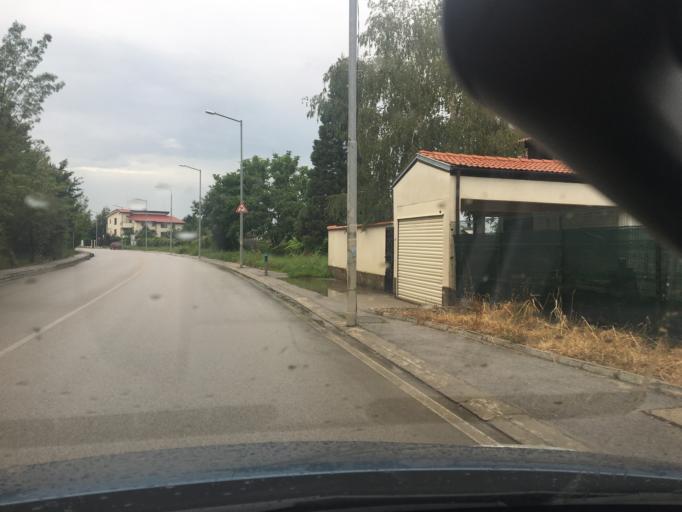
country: BG
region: Sofia-Capital
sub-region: Stolichna Obshtina
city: Sofia
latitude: 42.6419
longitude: 23.2926
